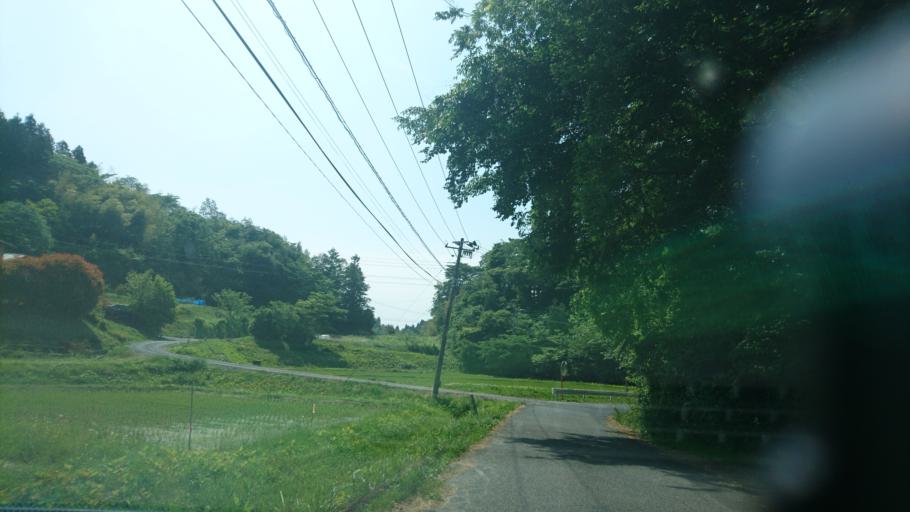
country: JP
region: Iwate
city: Ichinoseki
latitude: 38.8982
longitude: 141.3374
